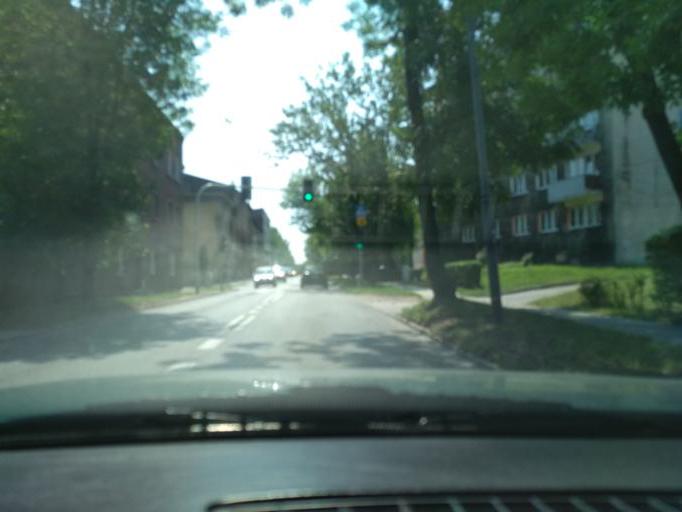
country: PL
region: Silesian Voivodeship
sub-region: Katowice
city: Katowice
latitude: 50.2863
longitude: 19.0068
